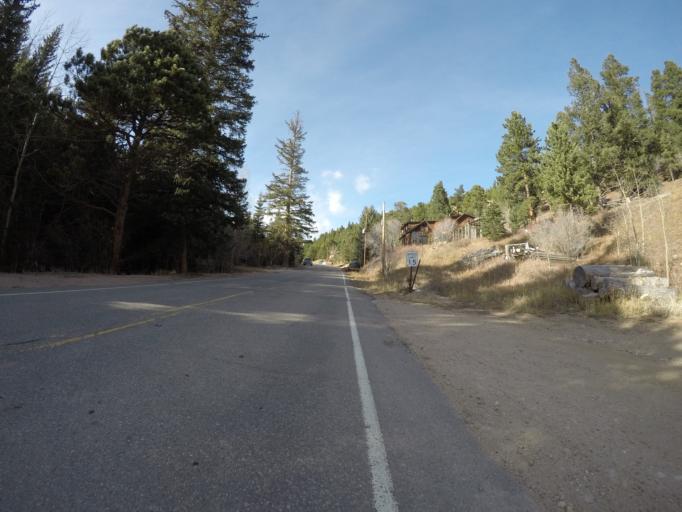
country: US
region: Colorado
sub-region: Boulder County
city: Nederland
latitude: 40.0690
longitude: -105.5046
